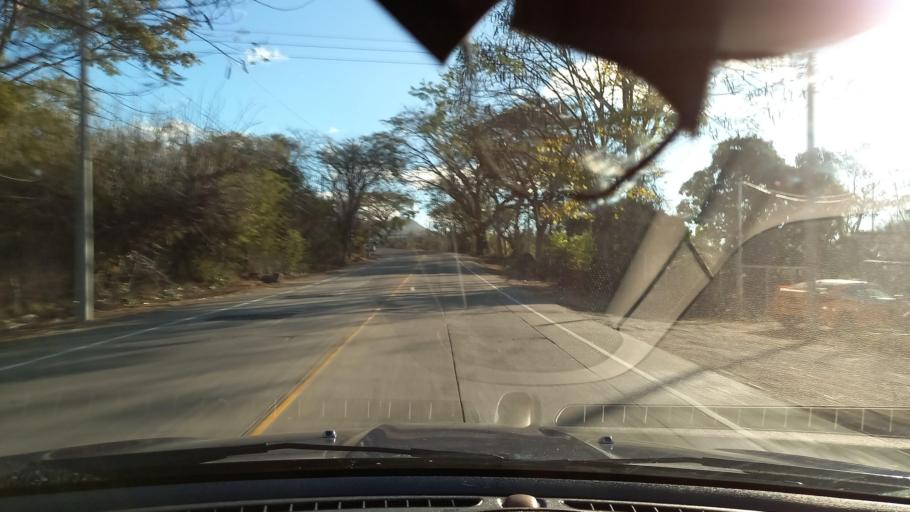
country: SV
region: Santa Ana
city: Texistepeque
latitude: 14.2227
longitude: -89.4846
